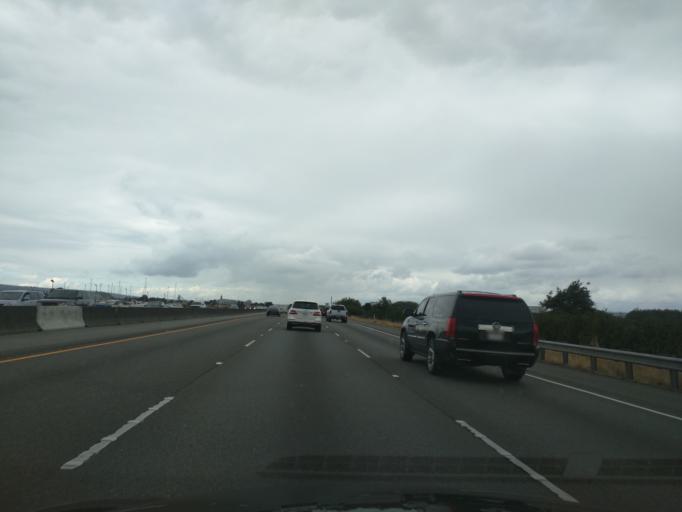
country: US
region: Washington
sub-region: Snohomish County
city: Marysville
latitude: 48.0122
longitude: -122.1745
